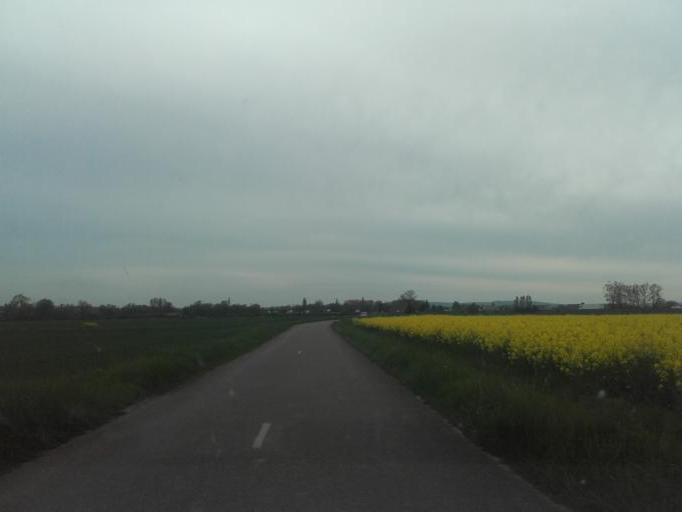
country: FR
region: Bourgogne
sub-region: Departement de Saone-et-Loire
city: Demigny
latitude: 46.9465
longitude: 4.8325
